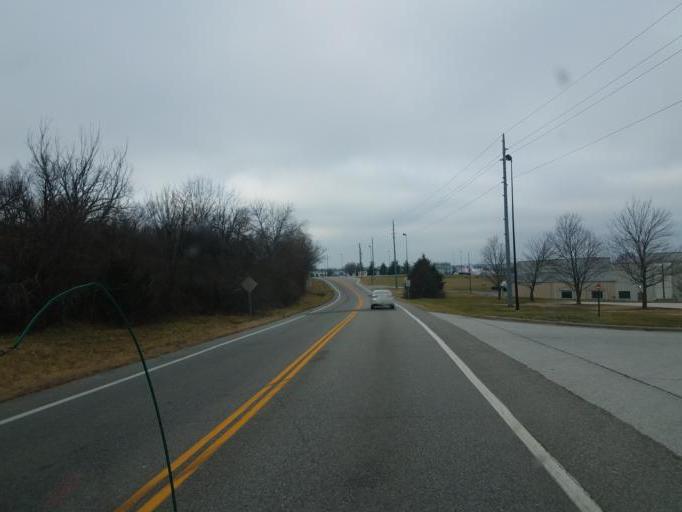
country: US
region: Missouri
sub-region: Greene County
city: Strafford
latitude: 37.2463
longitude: -93.1916
